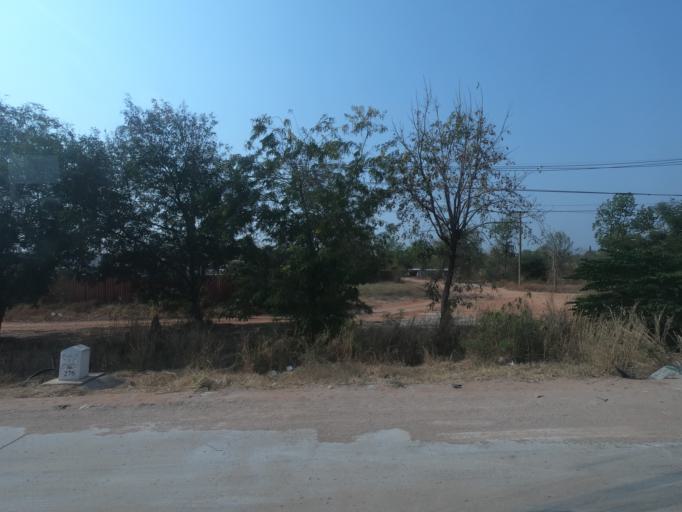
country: TH
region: Khon Kaen
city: Non Sila
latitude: 15.9138
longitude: 102.6598
